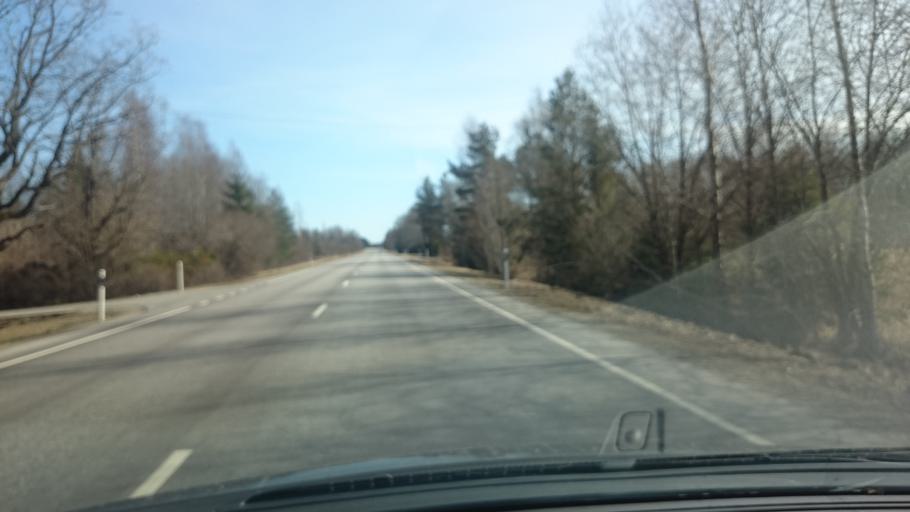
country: EE
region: Paernumaa
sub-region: Vaendra vald (alev)
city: Vandra
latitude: 58.6708
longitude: 25.1323
